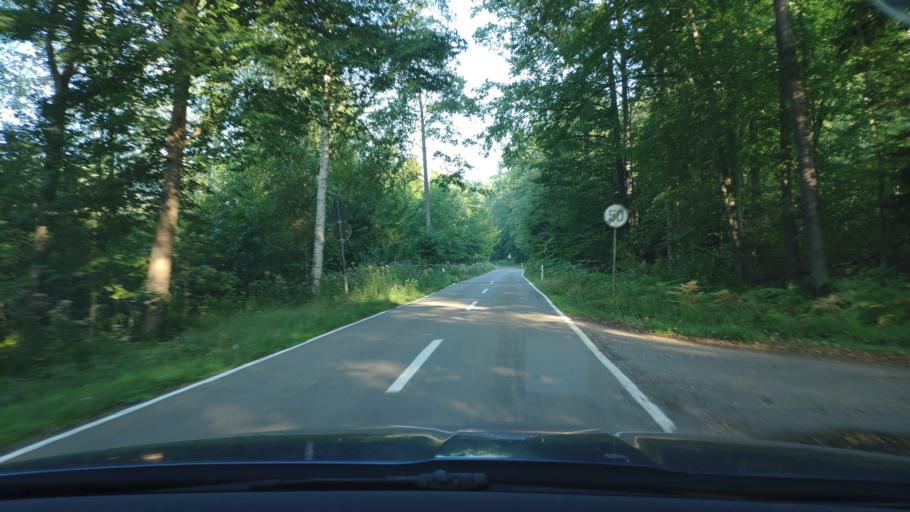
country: DE
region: Rheinland-Pfalz
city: Ludwigswinkel
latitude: 49.0877
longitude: 7.6560
